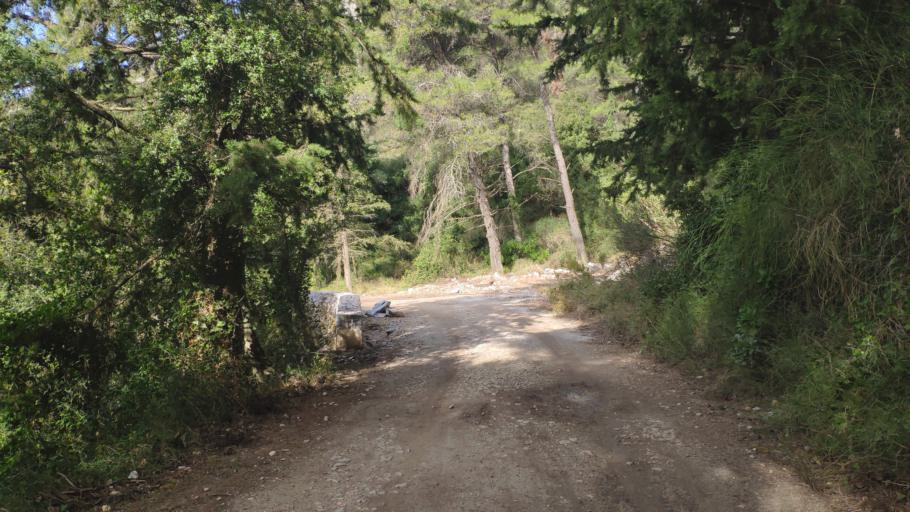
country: GR
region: Attica
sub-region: Nomarchia Anatolikis Attikis
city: Varybobi
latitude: 38.1646
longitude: 23.7858
